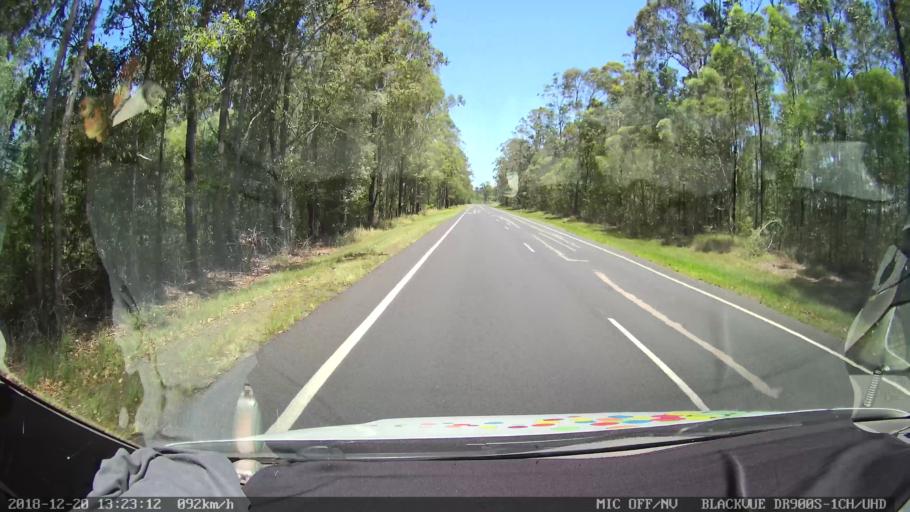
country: AU
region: New South Wales
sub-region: Richmond Valley
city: Casino
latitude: -29.1014
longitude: 153.0006
